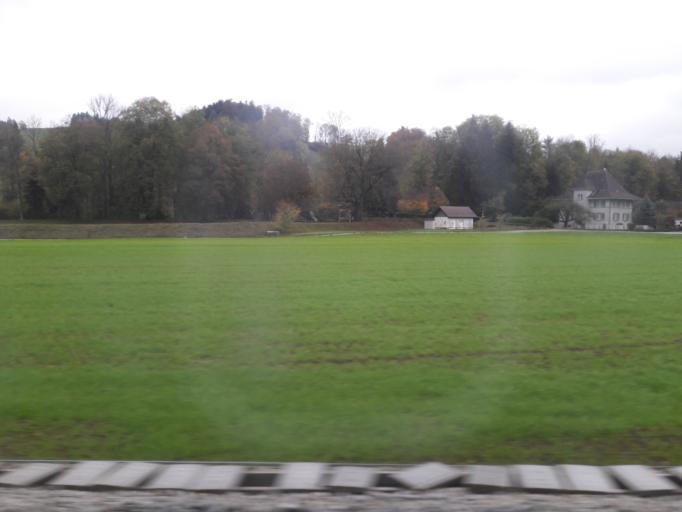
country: CH
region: Bern
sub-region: Emmental District
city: Oberburg
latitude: 47.0202
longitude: 7.6464
